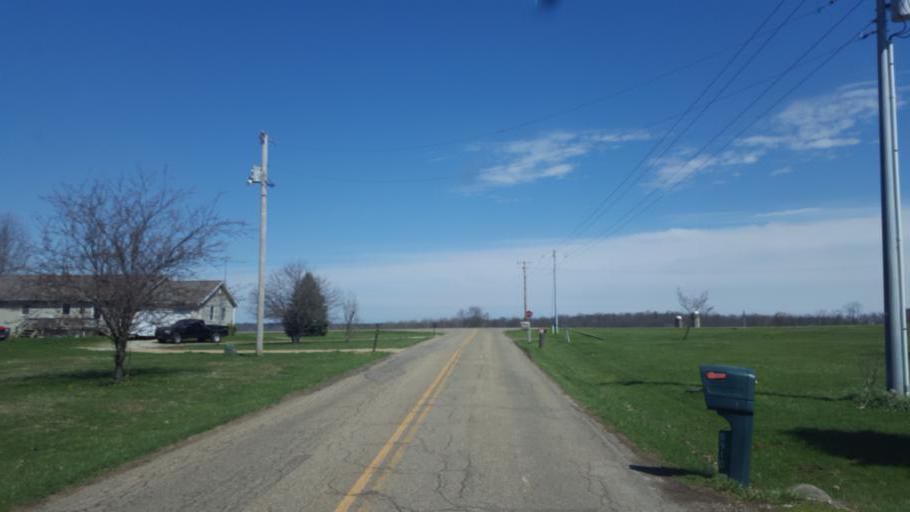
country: US
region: Ohio
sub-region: Knox County
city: Gambier
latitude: 40.3577
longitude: -82.3625
